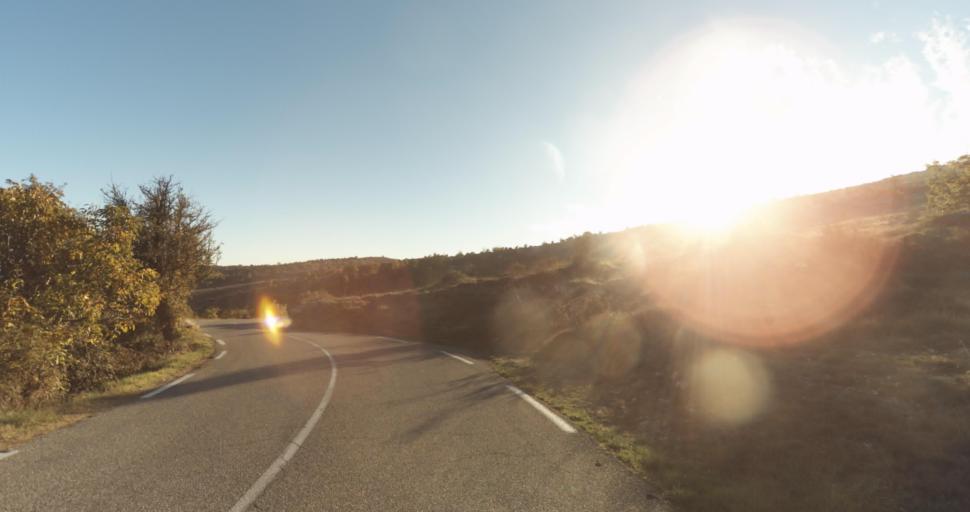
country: FR
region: Provence-Alpes-Cote d'Azur
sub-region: Departement des Alpes-Maritimes
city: Vence
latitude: 43.7588
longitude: 7.0866
